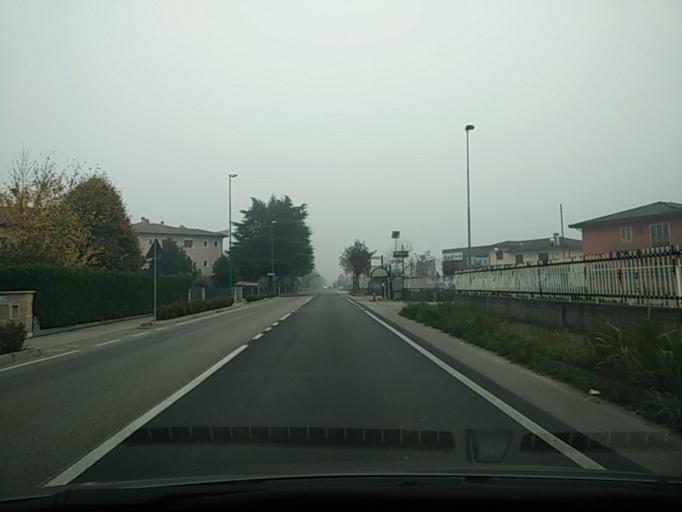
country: IT
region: Veneto
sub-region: Provincia di Venezia
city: Salzano
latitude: 45.5263
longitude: 12.0857
